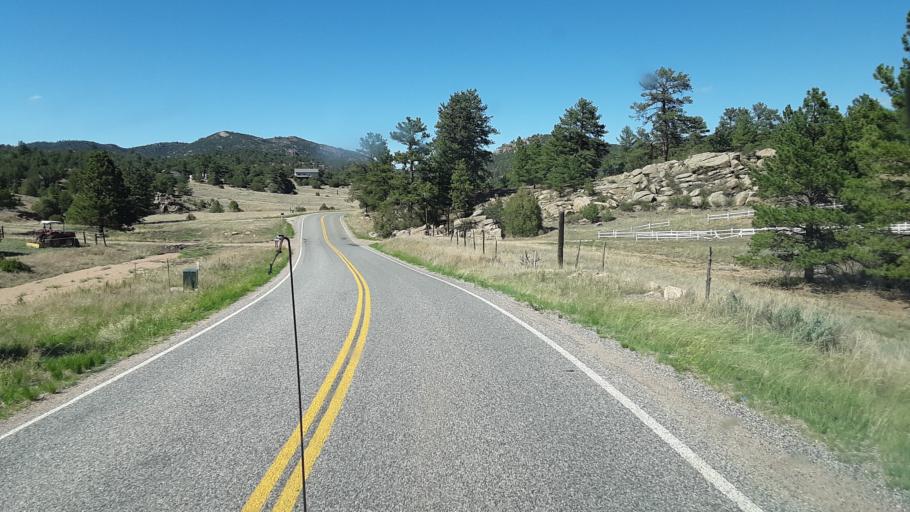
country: US
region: Colorado
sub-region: Custer County
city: Westcliffe
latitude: 38.3657
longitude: -105.4623
